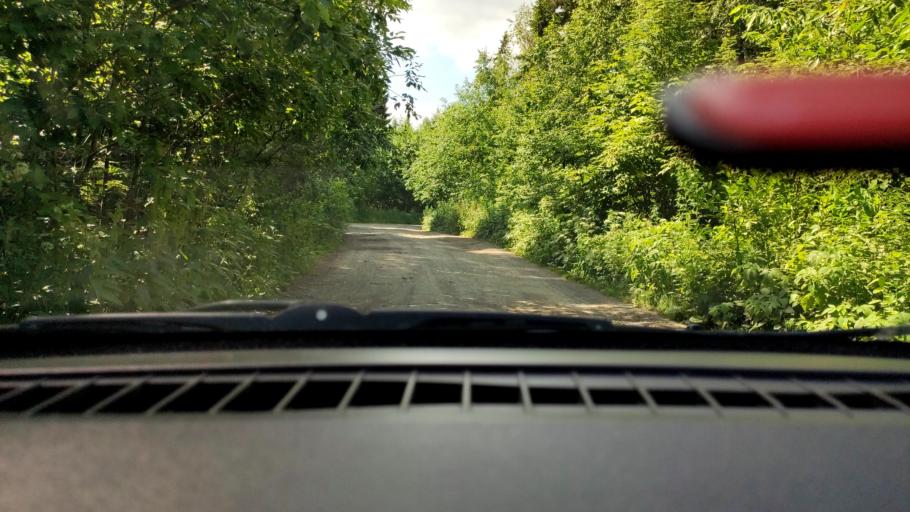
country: RU
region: Perm
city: Perm
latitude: 58.1487
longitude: 56.2970
